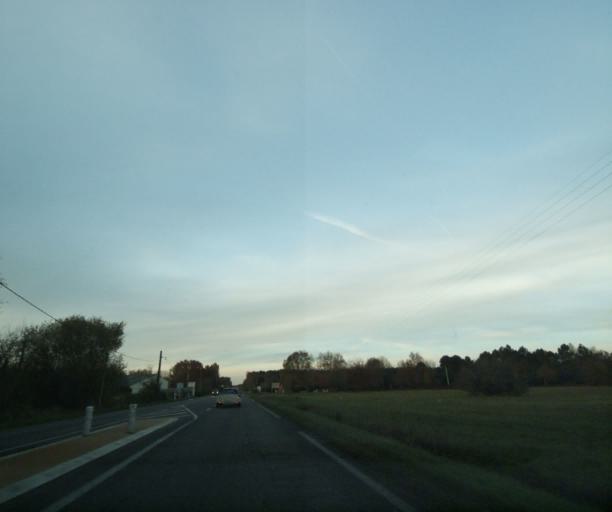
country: FR
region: Aquitaine
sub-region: Departement de la Gironde
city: Bazas
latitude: 44.4896
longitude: -0.2337
